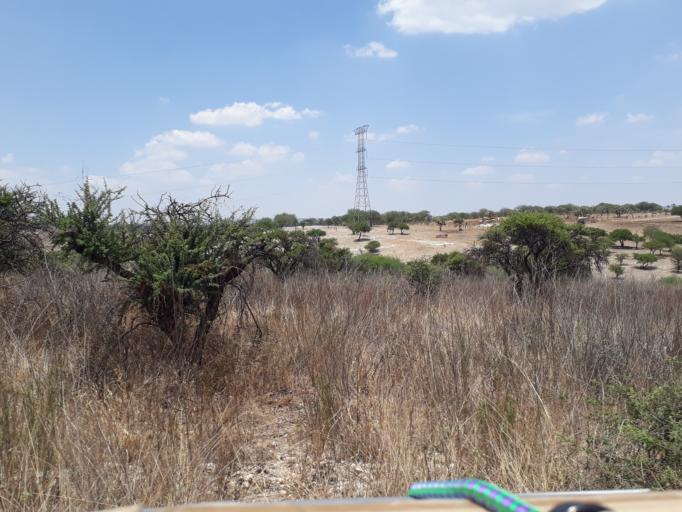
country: MX
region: Aguascalientes
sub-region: Aguascalientes
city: San Sebastian [Fraccionamiento]
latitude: 21.7825
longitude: -102.3290
